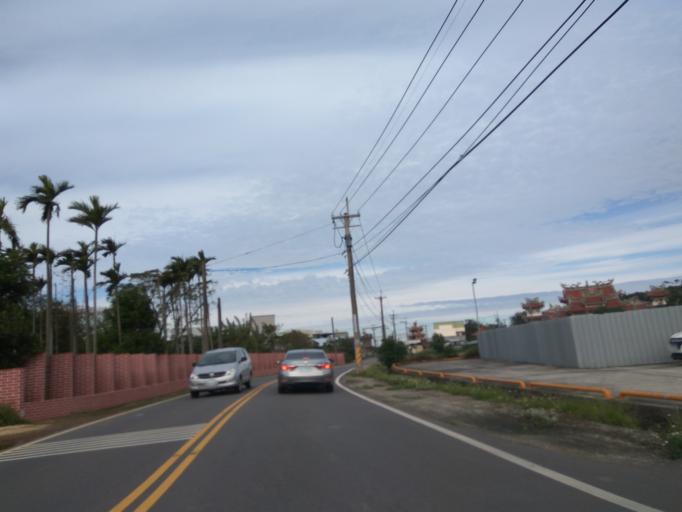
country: TW
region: Taiwan
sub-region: Hsinchu
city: Zhubei
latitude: 24.9587
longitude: 121.1185
